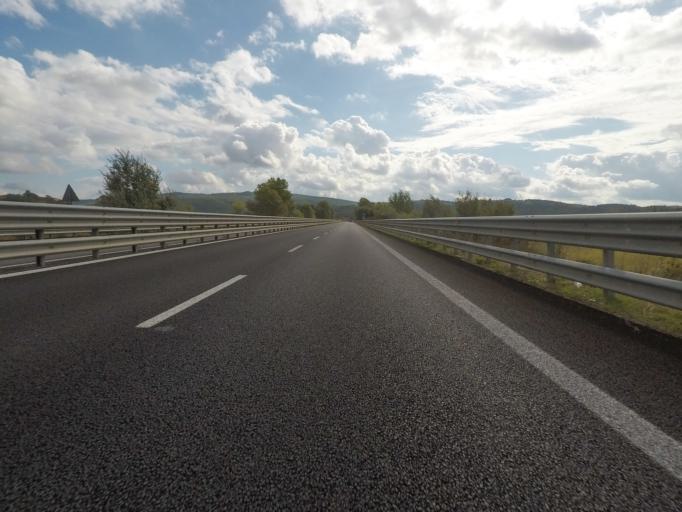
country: IT
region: Tuscany
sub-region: Provincia di Siena
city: Serre di Rapolano
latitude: 43.2507
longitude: 11.6409
